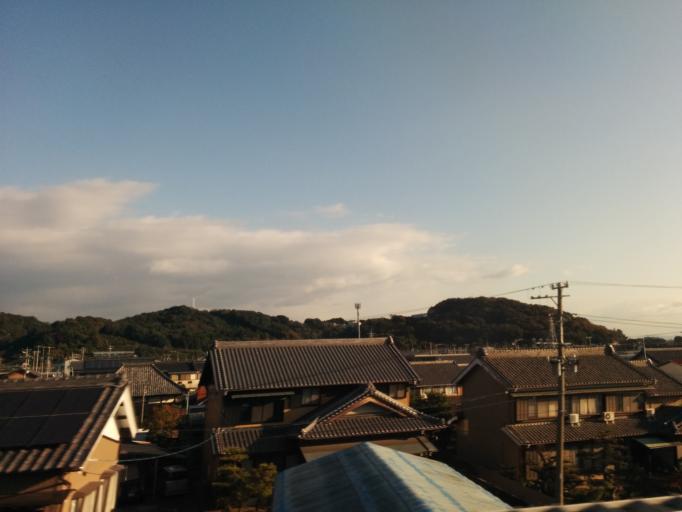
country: JP
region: Aichi
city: Kozakai-cho
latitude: 34.8123
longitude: 137.3011
